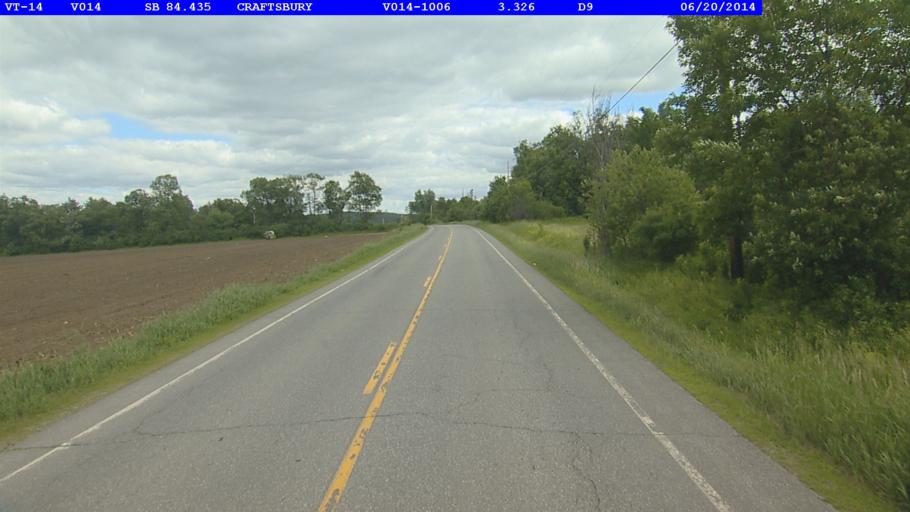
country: US
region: Vermont
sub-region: Caledonia County
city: Hardwick
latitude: 44.6393
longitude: -72.3999
